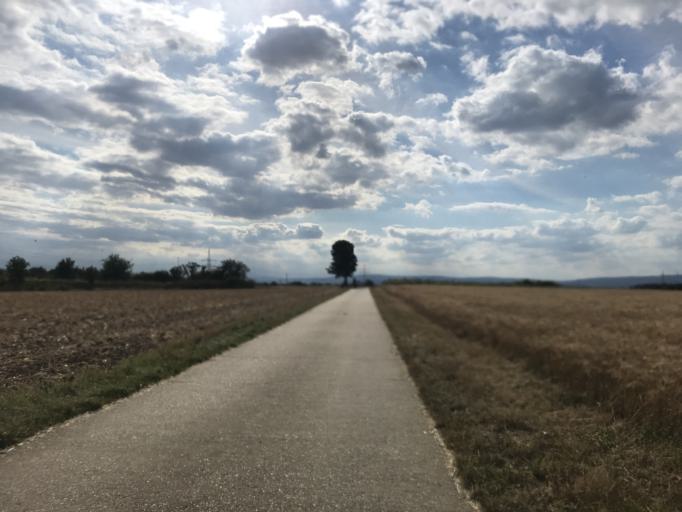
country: DE
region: Hesse
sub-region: Regierungsbezirk Darmstadt
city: Hochheim am Main
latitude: 50.0279
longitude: 8.3149
